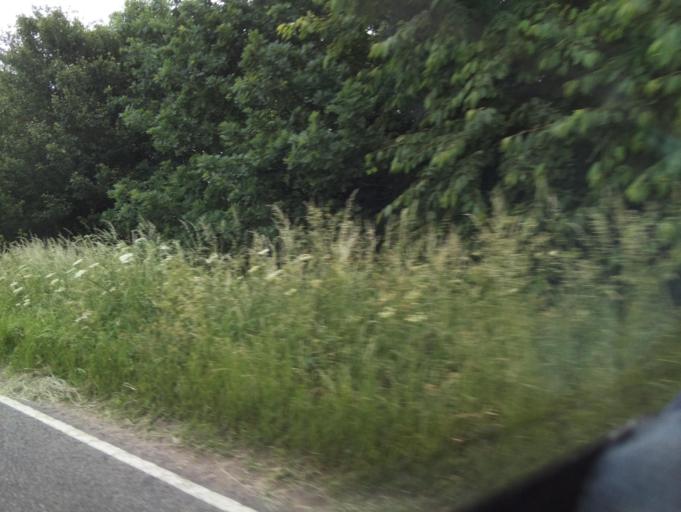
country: GB
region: England
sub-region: Leicestershire
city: Sileby
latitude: 52.8085
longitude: -1.0900
